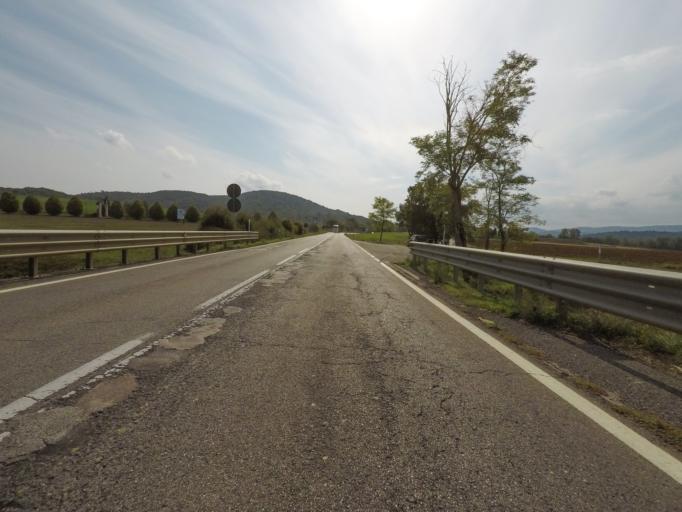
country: IT
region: Tuscany
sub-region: Provincia di Siena
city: Rosia
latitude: 43.2112
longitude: 11.2784
